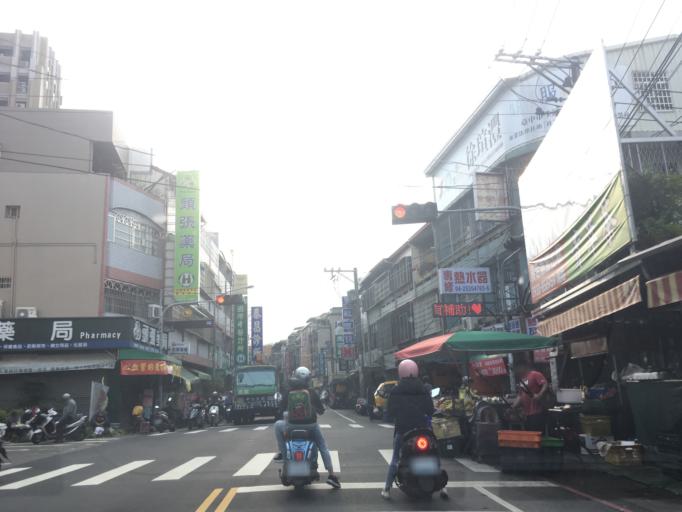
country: TW
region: Taiwan
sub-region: Taichung City
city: Taichung
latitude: 24.1944
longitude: 120.6994
